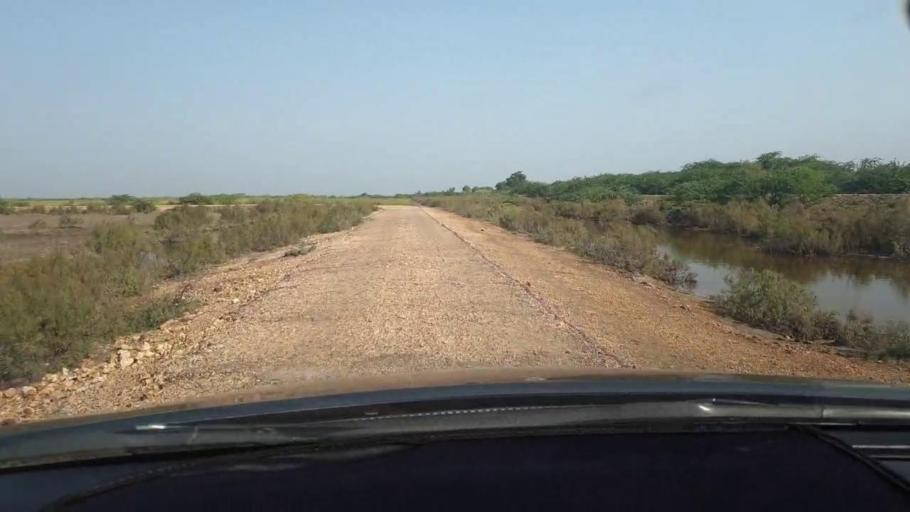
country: PK
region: Sindh
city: Tando Bago
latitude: 24.6789
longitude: 69.1687
